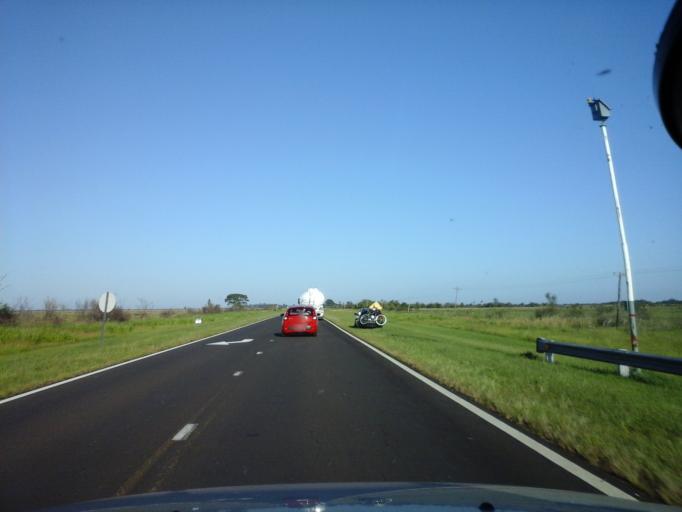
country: AR
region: Corrientes
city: Ita Ibate
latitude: -27.5018
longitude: -57.2504
